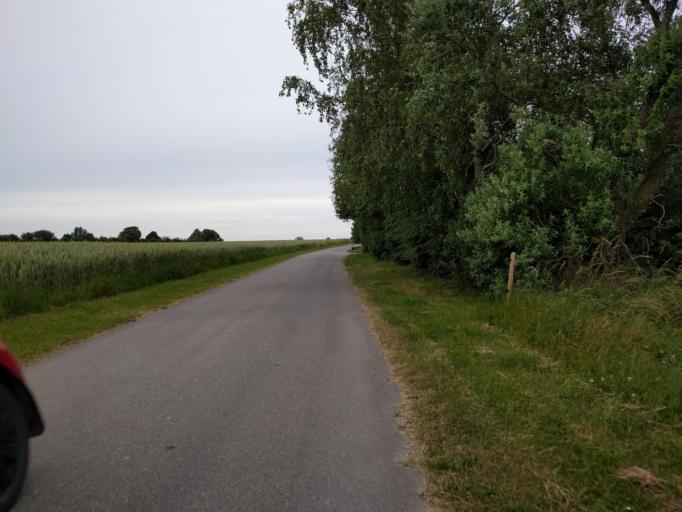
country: DK
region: South Denmark
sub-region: Kerteminde Kommune
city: Langeskov
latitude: 55.3959
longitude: 10.5941
